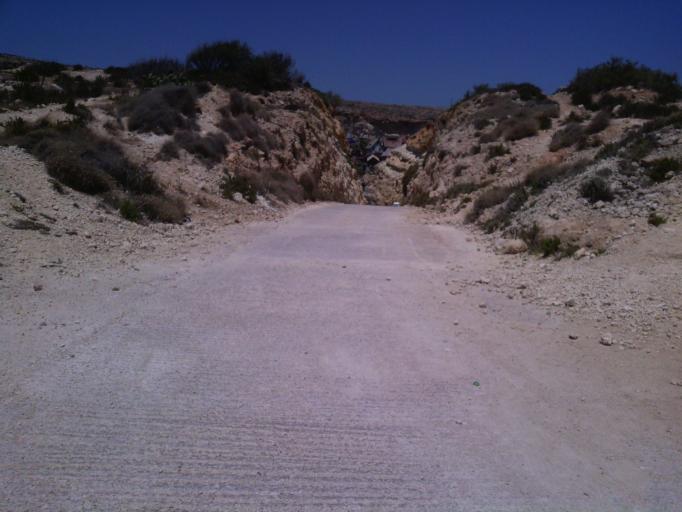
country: MT
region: Il-Mellieha
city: Mellieha
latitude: 35.9583
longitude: 14.3403
